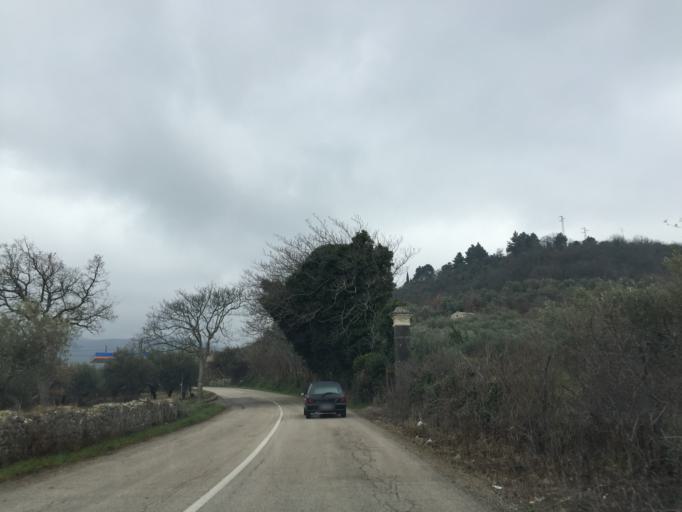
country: IT
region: Apulia
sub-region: Provincia di Foggia
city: Bovino
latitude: 41.2560
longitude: 15.3496
